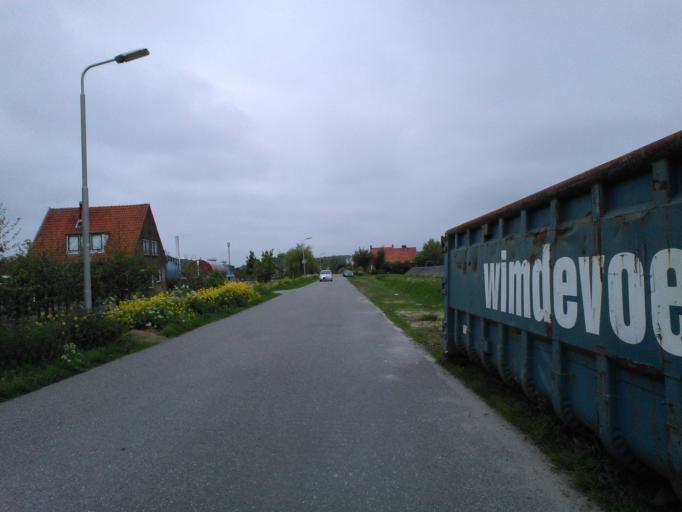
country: NL
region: South Holland
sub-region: Gemeente Pijnacker-Nootdorp
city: Pijnacker
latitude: 52.0462
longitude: 4.4293
